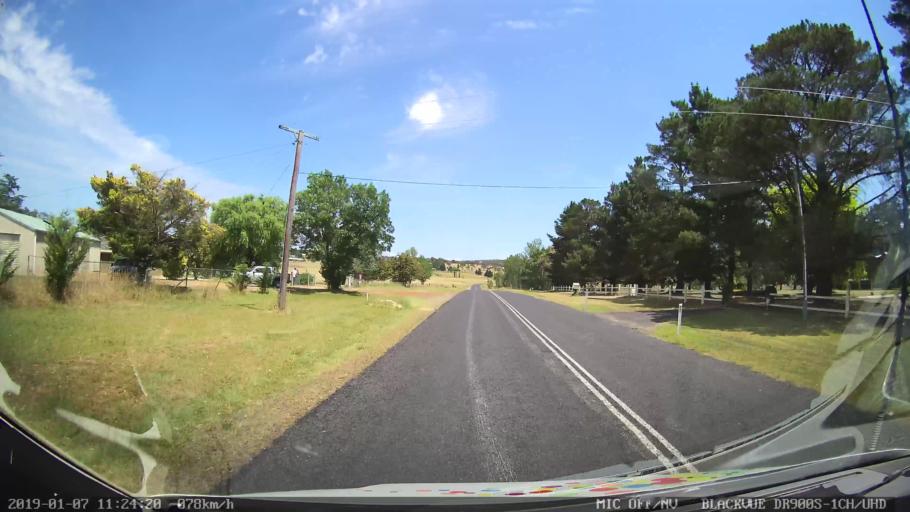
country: AU
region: New South Wales
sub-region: Armidale Dumaresq
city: Armidale
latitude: -30.4677
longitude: 151.6127
